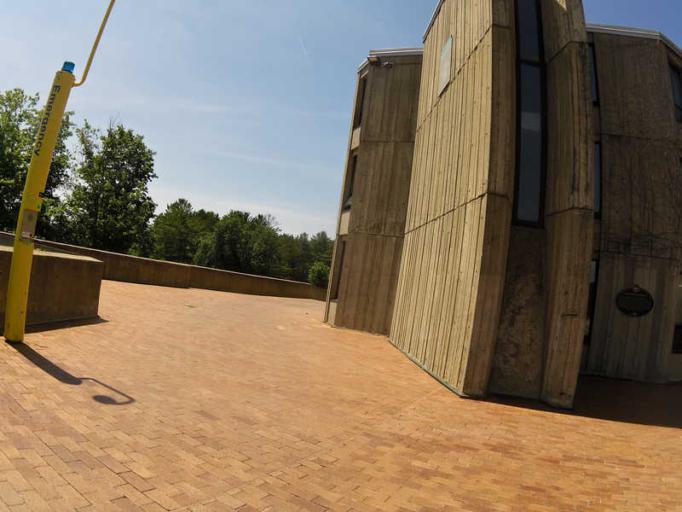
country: CA
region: Ontario
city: Peterborough
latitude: 44.3580
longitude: -78.2918
